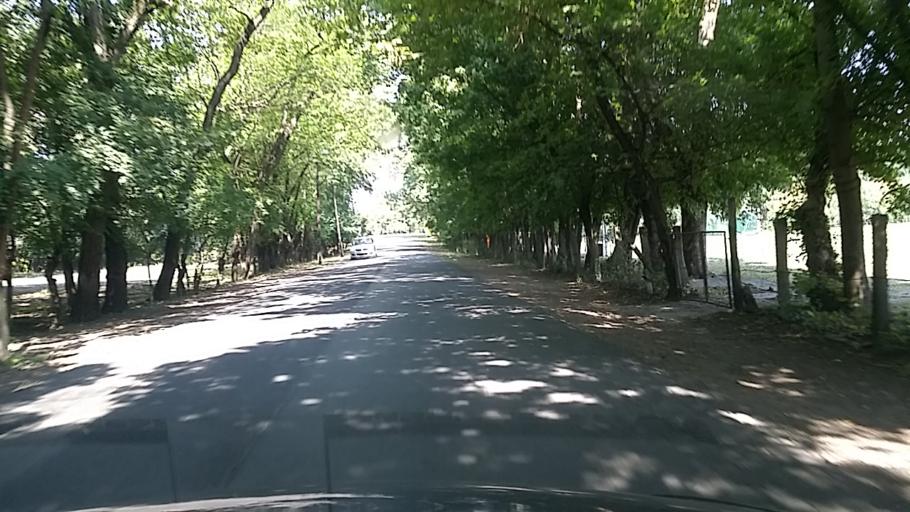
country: HU
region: Bekes
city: Gyomaendrod
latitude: 46.9393
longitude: 20.8381
